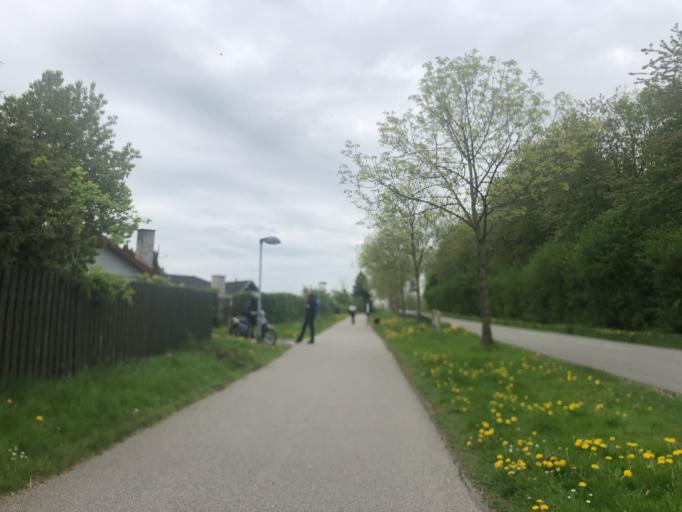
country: DK
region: Zealand
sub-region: Koge Kommune
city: Bjaeverskov
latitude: 55.4570
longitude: 12.0275
